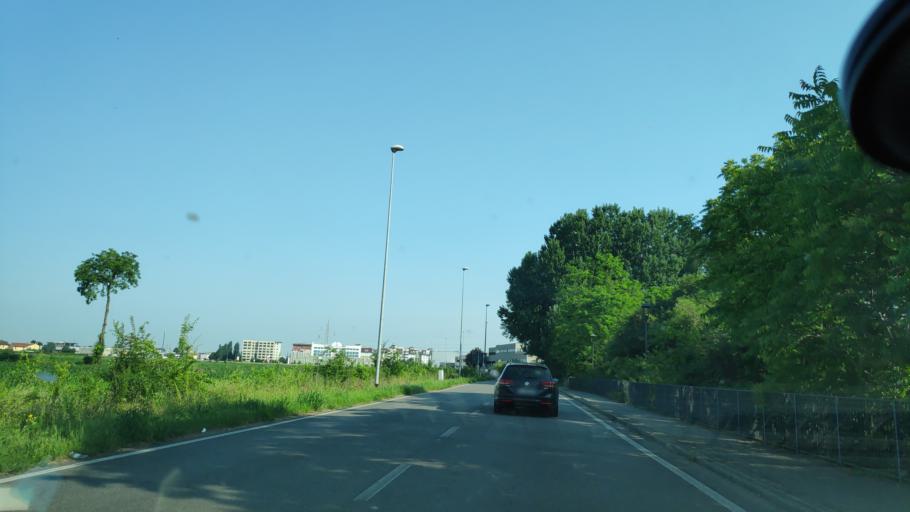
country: IT
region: Lombardy
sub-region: Citta metropolitana di Milano
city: Locate di Triulzi
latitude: 45.3653
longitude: 9.2182
